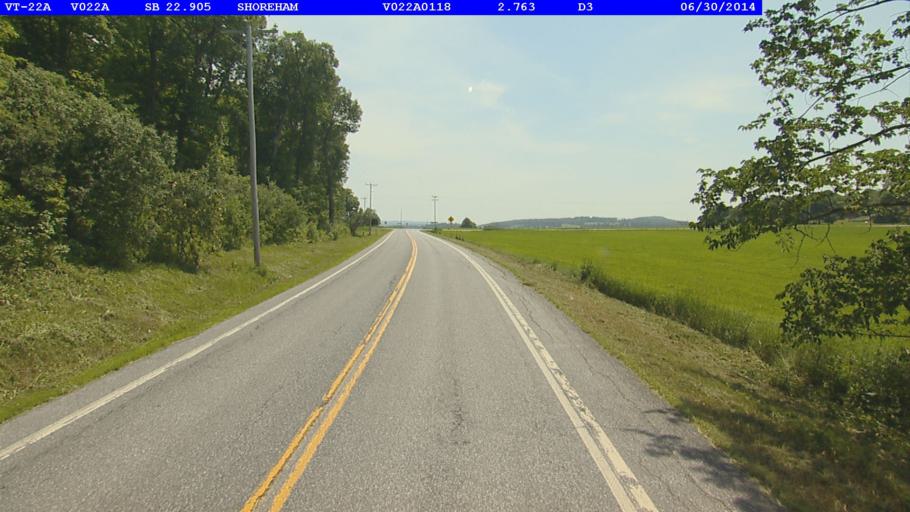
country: US
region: New York
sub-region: Essex County
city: Ticonderoga
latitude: 43.8893
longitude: -73.3097
